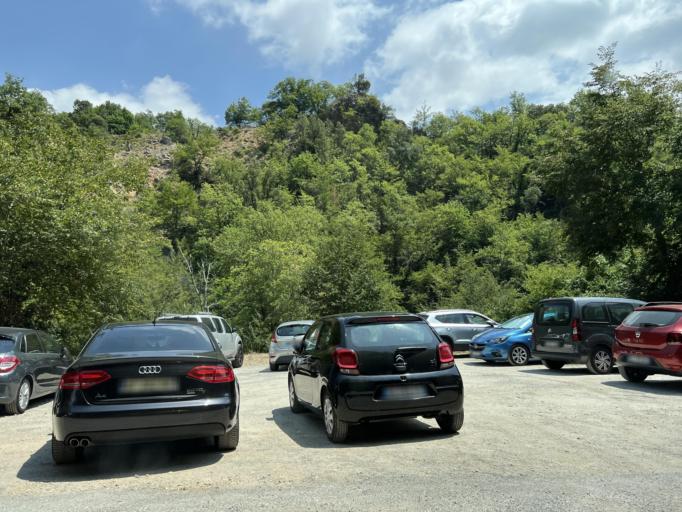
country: FR
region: Provence-Alpes-Cote d'Azur
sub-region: Departement des Alpes-Maritimes
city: Tourrettes-sur-Loup
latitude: 43.7518
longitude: 6.9935
